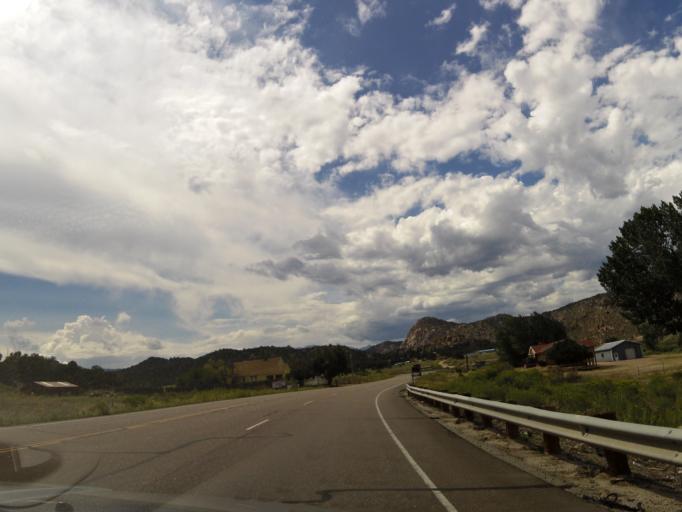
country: US
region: Colorado
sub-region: Custer County
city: Westcliffe
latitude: 38.3927
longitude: -105.6229
